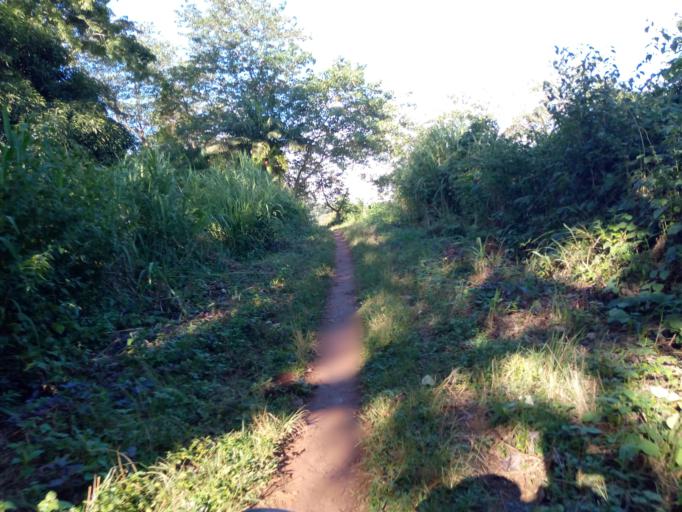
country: SL
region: Eastern Province
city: Buedu
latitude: 8.4773
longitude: -10.3356
